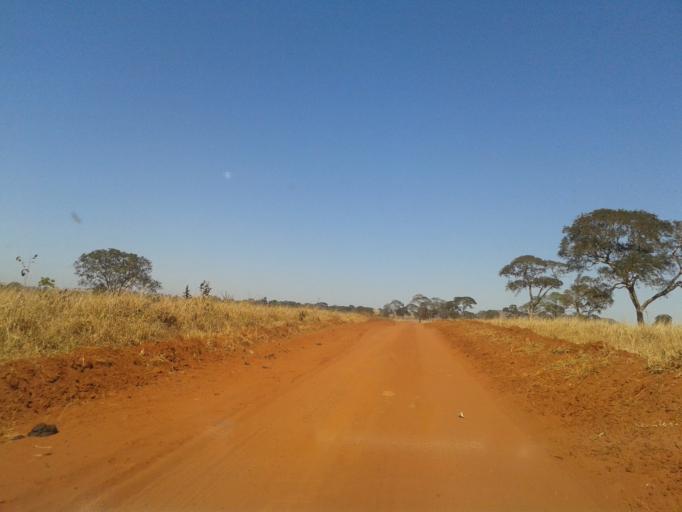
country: BR
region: Minas Gerais
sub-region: Santa Vitoria
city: Santa Vitoria
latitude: -19.1581
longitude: -50.1563
